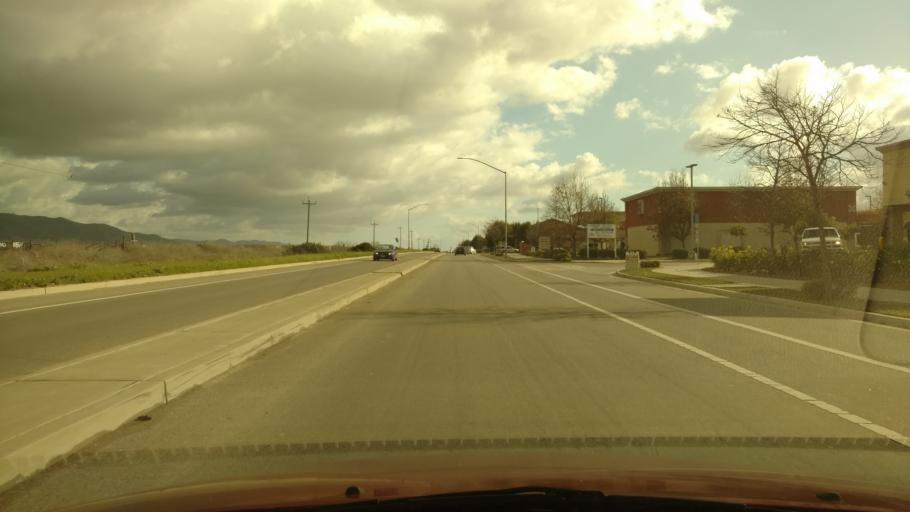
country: US
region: California
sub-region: Monterey County
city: Salinas
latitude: 36.6962
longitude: -121.5968
